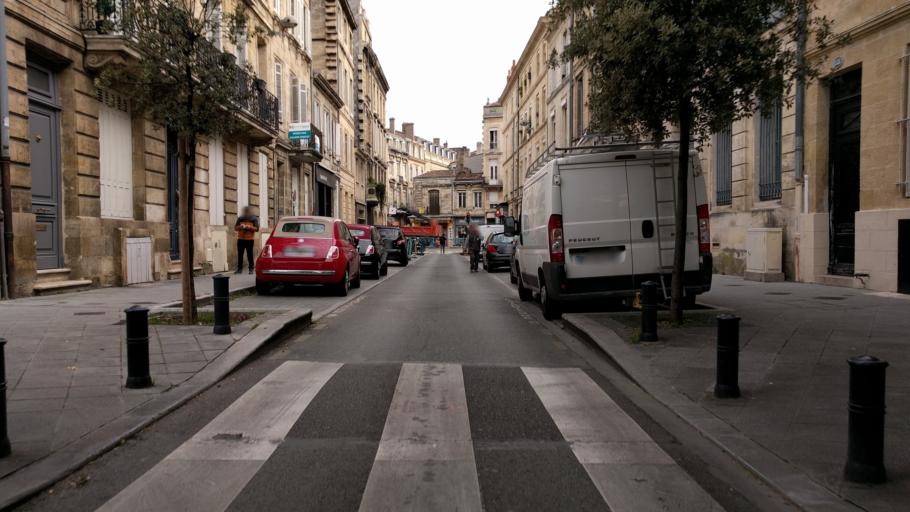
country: FR
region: Aquitaine
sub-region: Departement de la Gironde
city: Bordeaux
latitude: 44.8469
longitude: -0.5817
